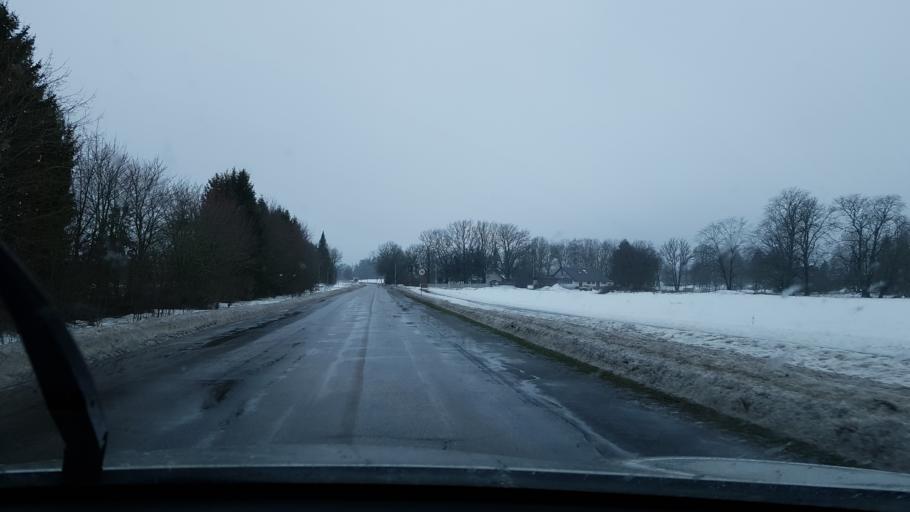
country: EE
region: Raplamaa
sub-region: Kohila vald
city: Kohila
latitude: 59.1629
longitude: 24.6759
